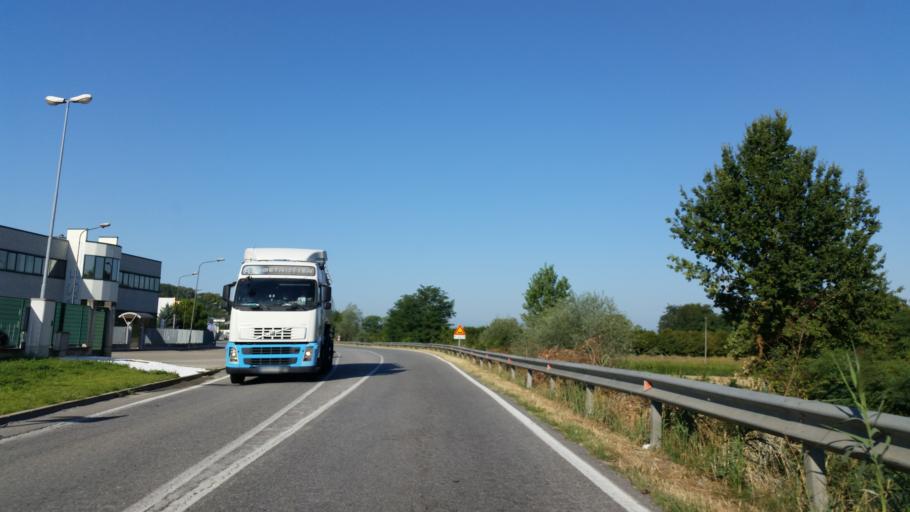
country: IT
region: Piedmont
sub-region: Provincia di Cuneo
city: Santa Vittoria d'Alba
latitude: 44.6834
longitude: 7.9395
